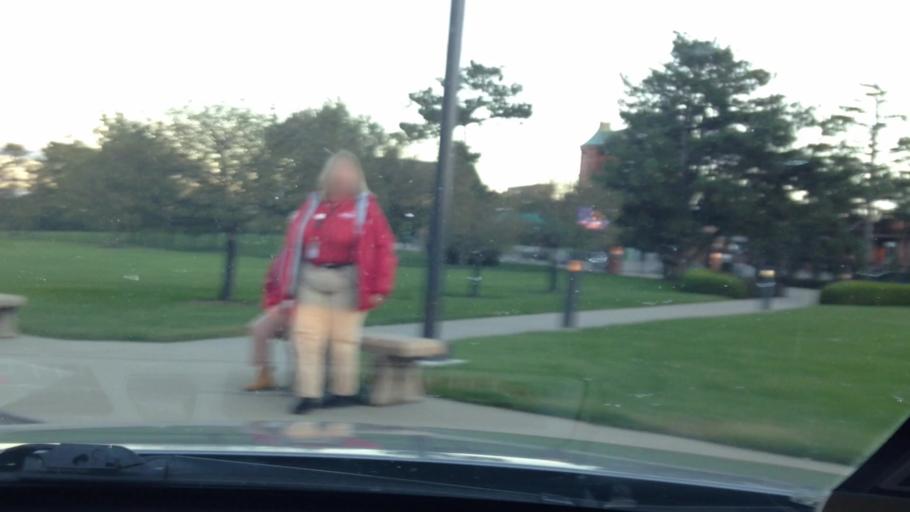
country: US
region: Missouri
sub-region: Jackson County
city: Raytown
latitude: 39.0085
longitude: -94.5341
